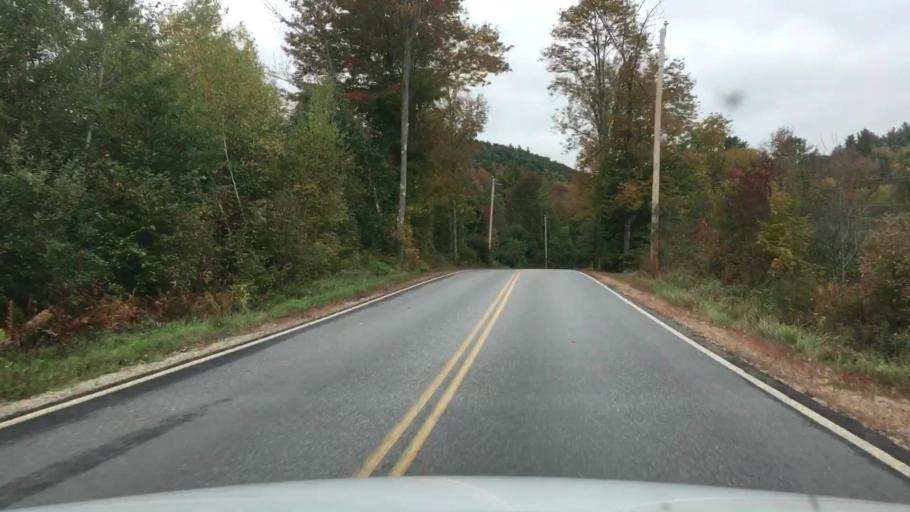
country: US
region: Maine
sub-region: Oxford County
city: Bethel
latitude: 44.2790
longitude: -70.7327
